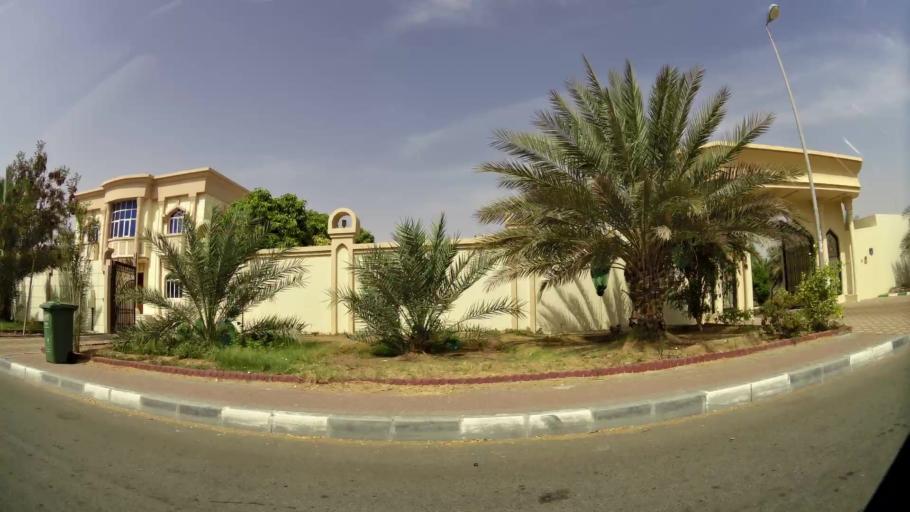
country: AE
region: Abu Dhabi
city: Al Ain
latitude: 24.1617
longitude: 55.6836
